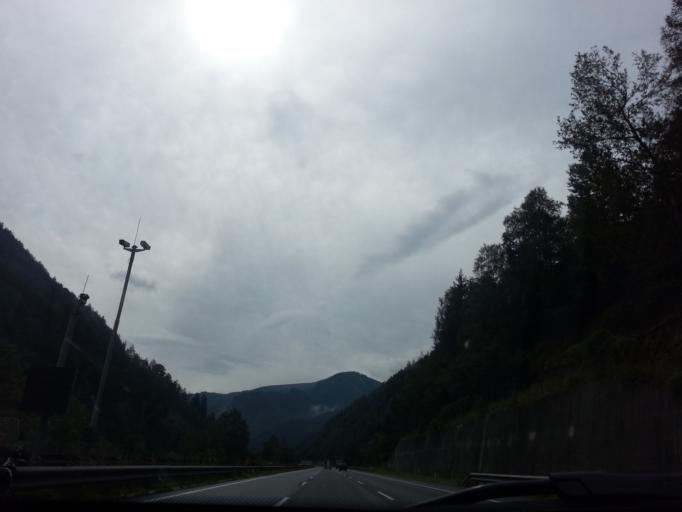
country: AT
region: Styria
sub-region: Politischer Bezirk Leoben
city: Sankt Michael in Obersteiermark
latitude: 47.3106
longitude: 15.0569
